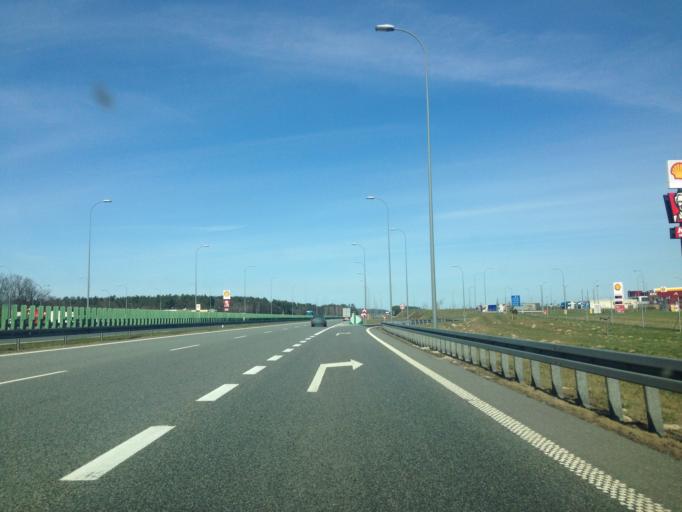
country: PL
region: Pomeranian Voivodeship
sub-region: Powiat starogardzki
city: Bobowo
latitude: 53.8859
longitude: 18.6296
